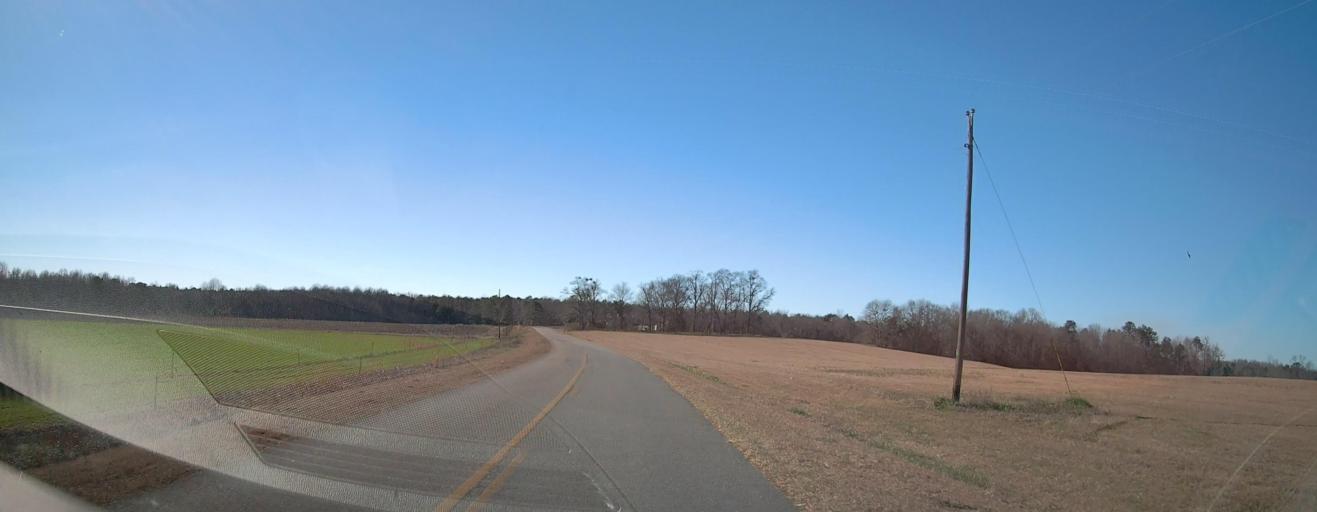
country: US
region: Georgia
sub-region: Taylor County
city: Butler
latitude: 32.6432
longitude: -84.3090
